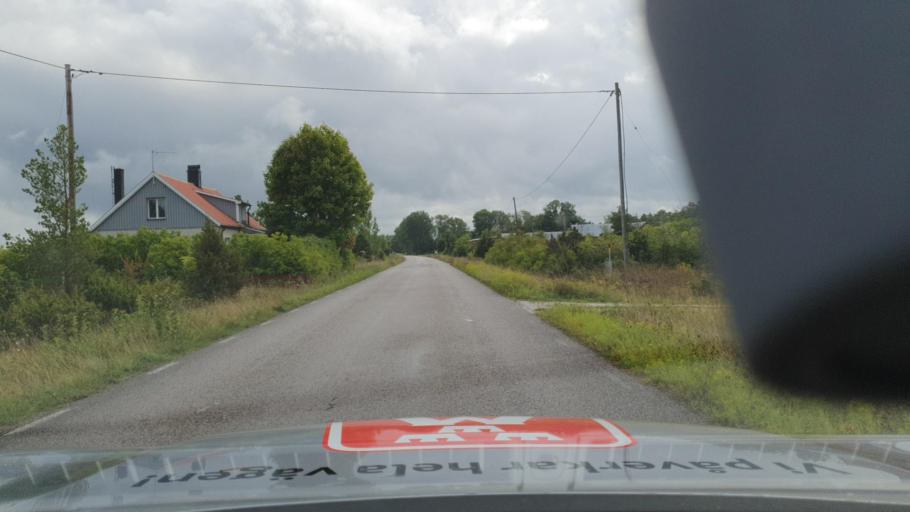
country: SE
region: Gotland
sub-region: Gotland
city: Slite
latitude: 57.7058
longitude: 18.7577
